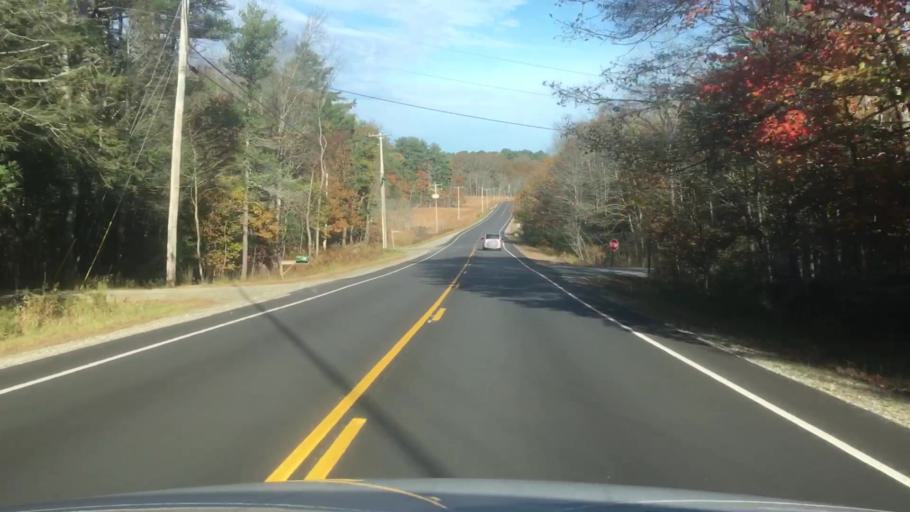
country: US
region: Maine
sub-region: Sagadahoc County
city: Woolwich
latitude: 43.8992
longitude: -69.7957
